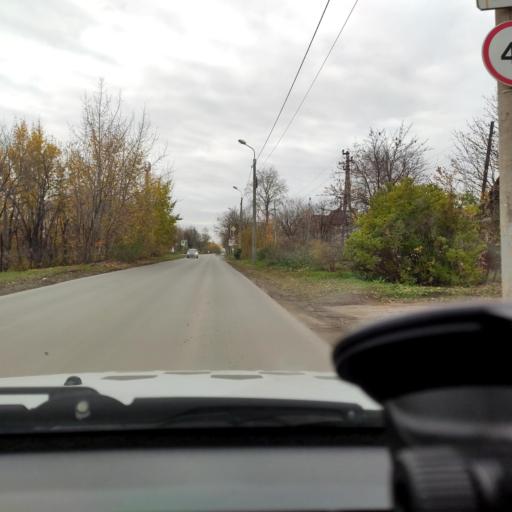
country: RU
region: Perm
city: Perm
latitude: 57.9932
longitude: 56.3081
